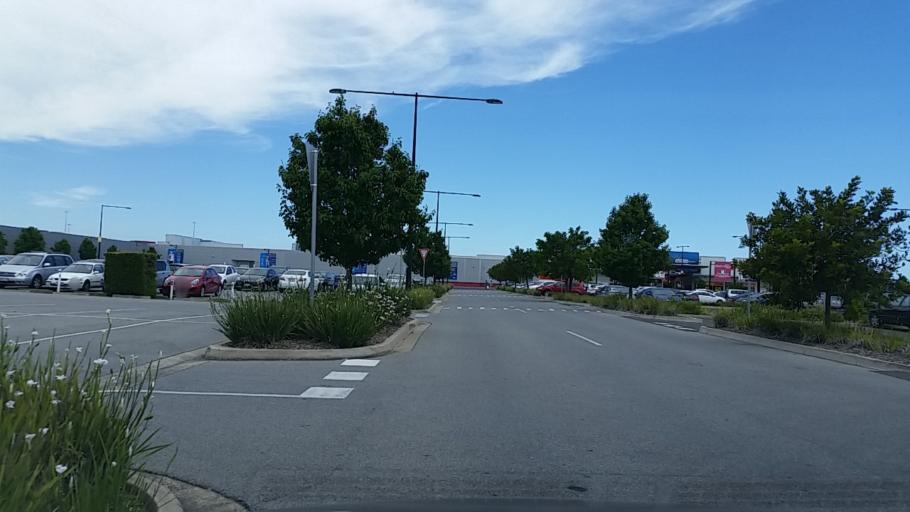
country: AU
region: South Australia
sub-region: City of West Torrens
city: Plympton
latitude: -34.9471
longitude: 138.5193
